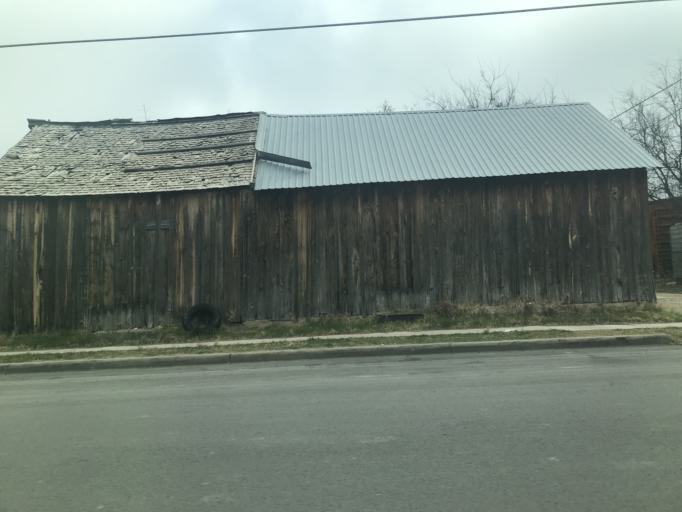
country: US
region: Texas
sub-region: Tom Green County
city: San Angelo
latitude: 31.4706
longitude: -100.4470
